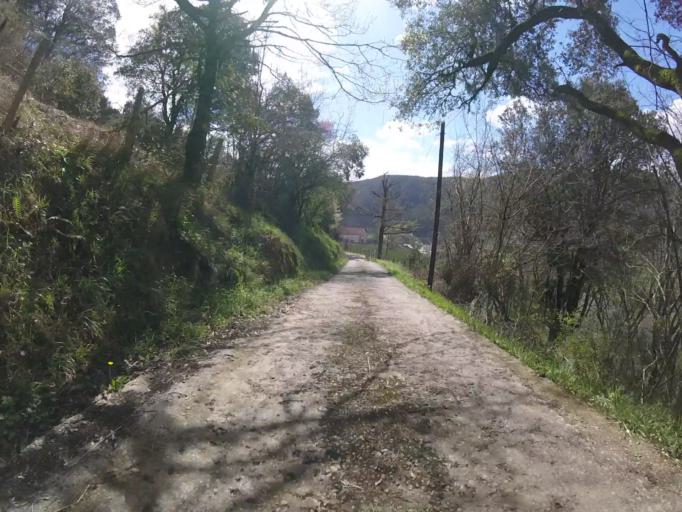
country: ES
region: Basque Country
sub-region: Provincia de Guipuzcoa
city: Albiztur
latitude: 43.1343
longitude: -2.1272
